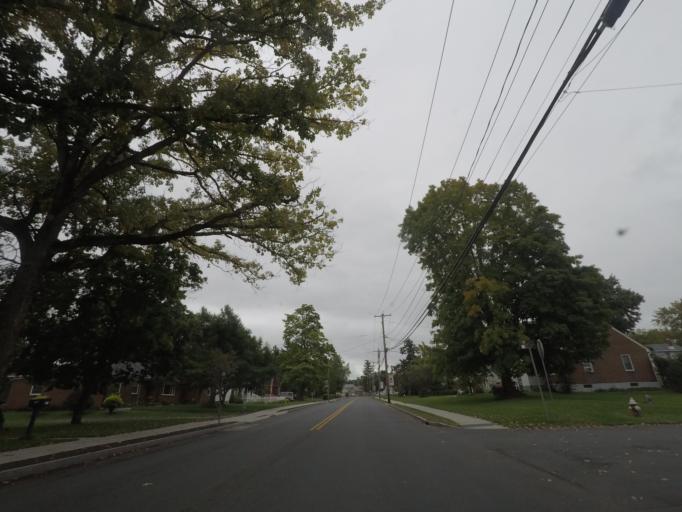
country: US
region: New York
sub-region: Rensselaer County
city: Rensselaer
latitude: 42.6563
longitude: -73.7108
